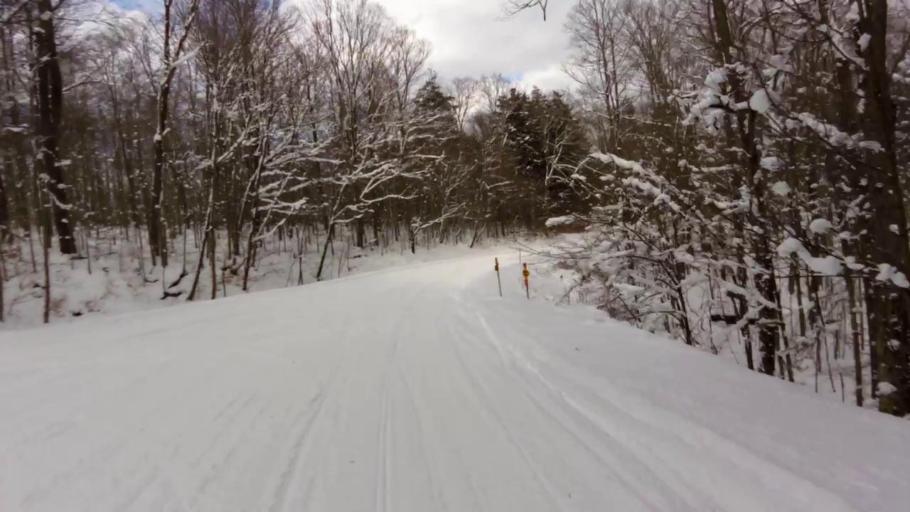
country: US
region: New York
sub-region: Cattaraugus County
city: Salamanca
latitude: 42.0536
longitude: -78.7657
